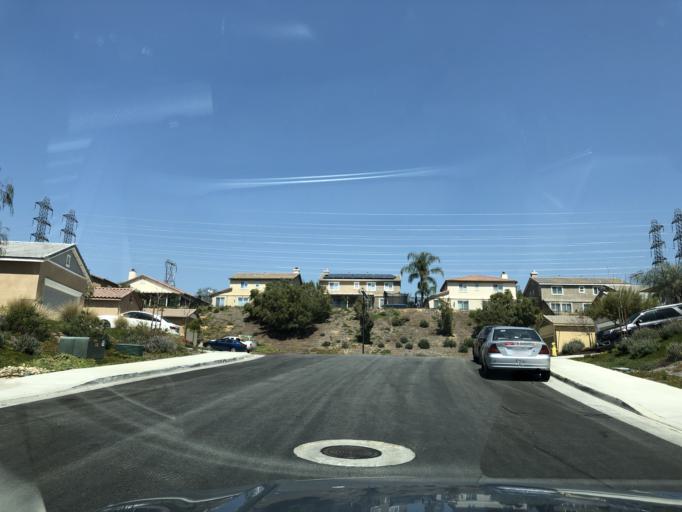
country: US
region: California
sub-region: Riverside County
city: Calimesa
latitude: 33.9617
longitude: -117.0469
